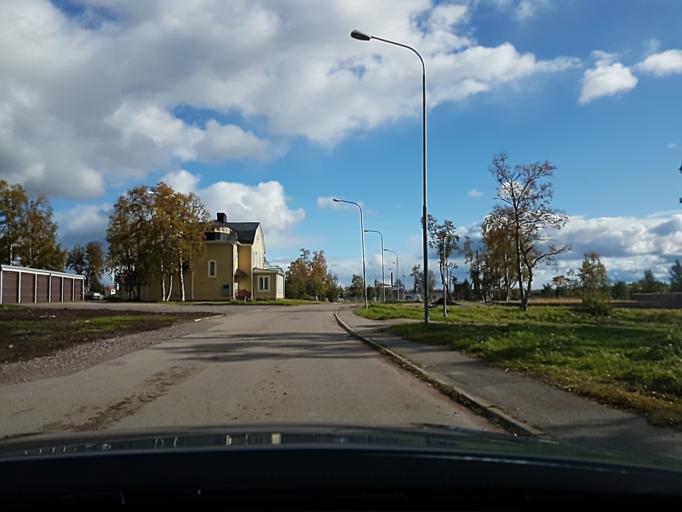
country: SE
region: Norrbotten
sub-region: Kiruna Kommun
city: Kiruna
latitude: 67.8469
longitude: 20.2248
